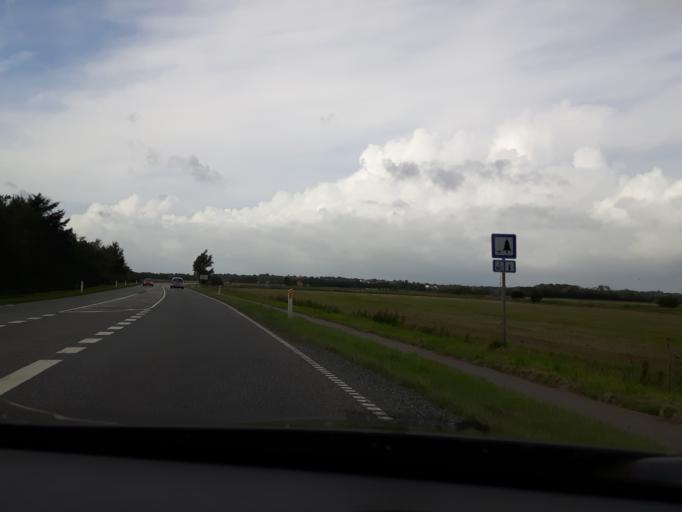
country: DK
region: North Denmark
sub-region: Jammerbugt Kommune
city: Brovst
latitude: 57.1043
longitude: 9.5604
